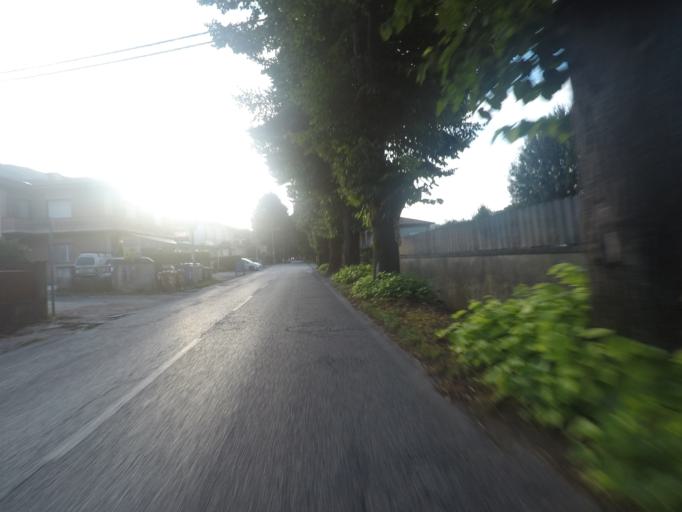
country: IT
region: Tuscany
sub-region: Provincia di Lucca
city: Corsanico-Bargecchia
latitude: 43.9279
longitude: 10.3163
